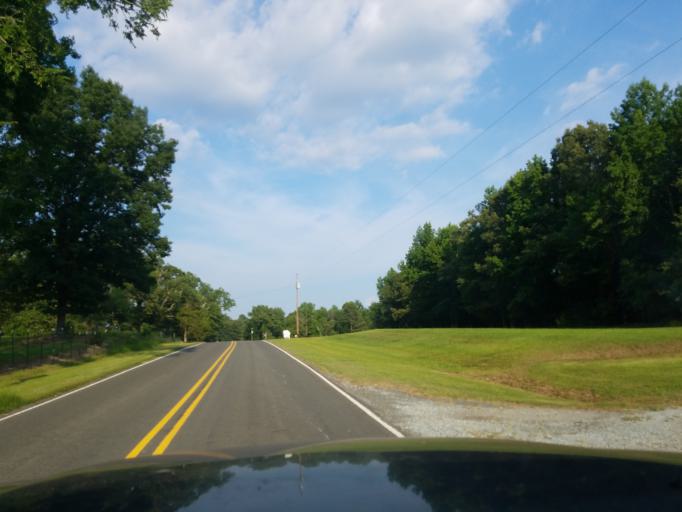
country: US
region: North Carolina
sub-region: Granville County
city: Butner
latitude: 36.1948
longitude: -78.8348
